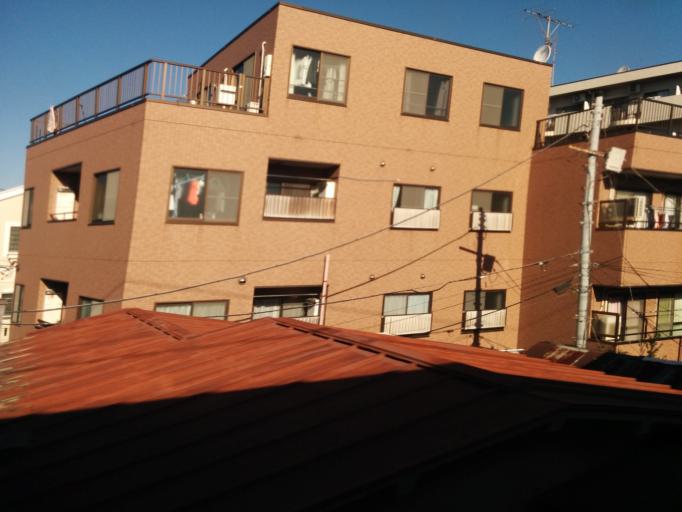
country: JP
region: Kanagawa
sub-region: Kawasaki-shi
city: Kawasaki
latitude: 35.5824
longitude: 139.6742
